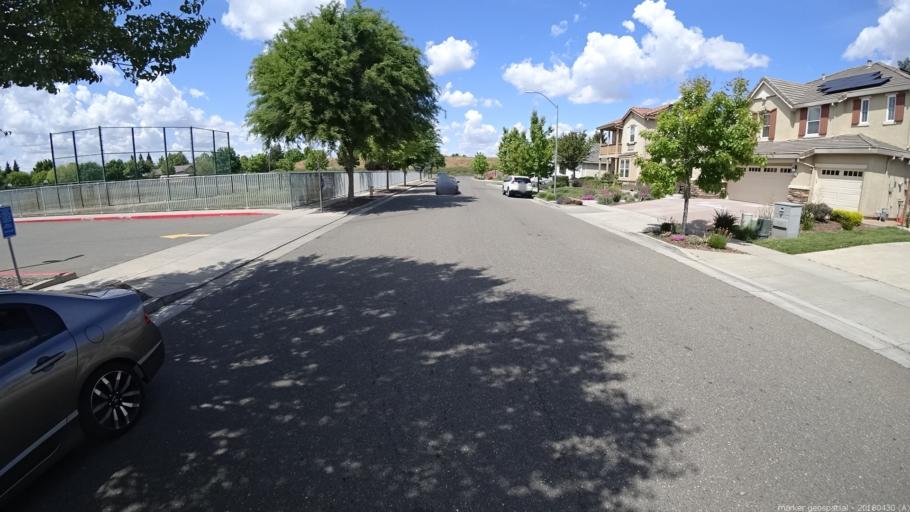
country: US
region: California
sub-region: Yolo County
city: West Sacramento
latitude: 38.5529
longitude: -121.5239
